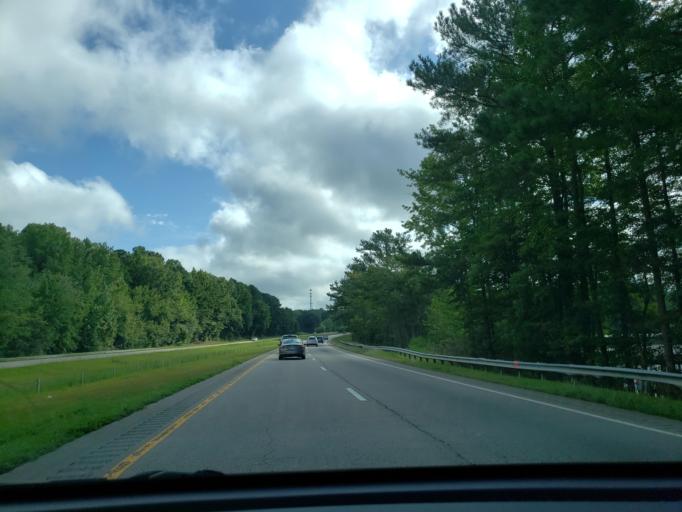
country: US
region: North Carolina
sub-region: Wake County
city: Zebulon
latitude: 35.8565
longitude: -78.2797
